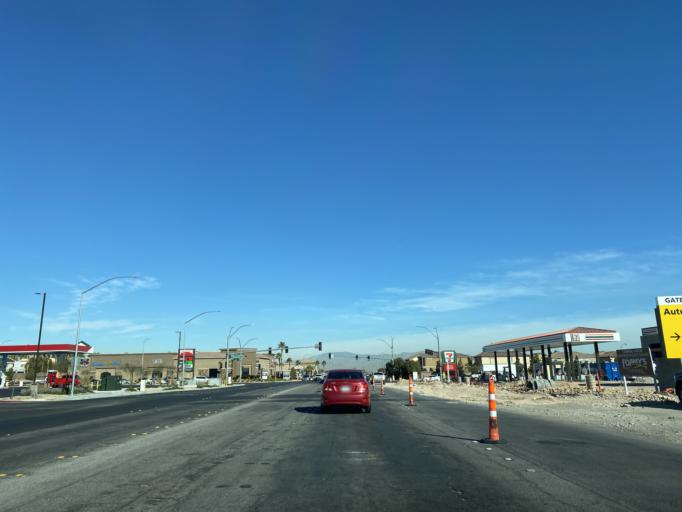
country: US
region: Nevada
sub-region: Clark County
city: Spring Valley
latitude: 36.0843
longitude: -115.2252
